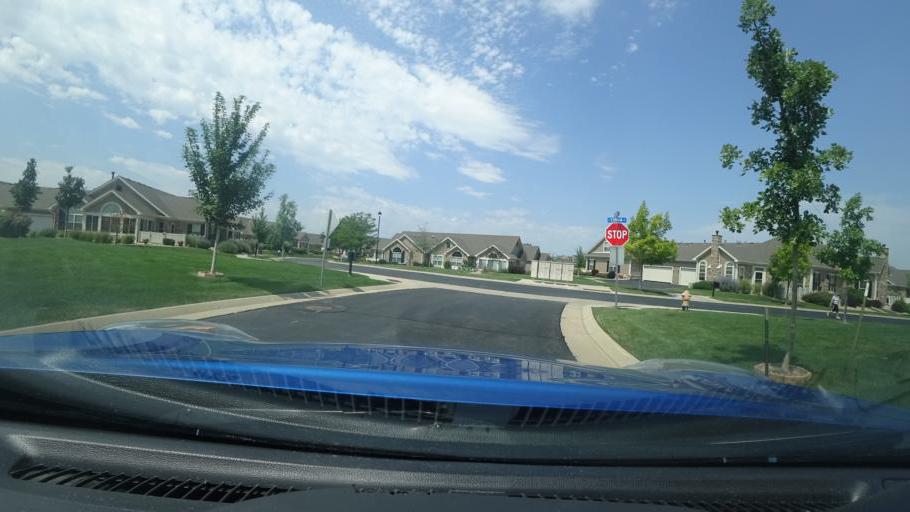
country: US
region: Colorado
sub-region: Adams County
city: Aurora
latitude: 39.6799
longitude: -104.7605
